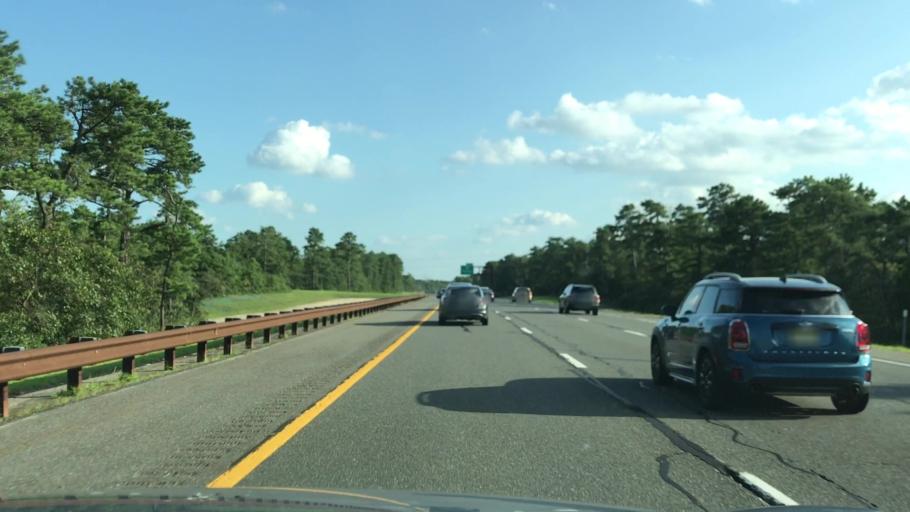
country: US
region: New Jersey
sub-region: Ocean County
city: Forked River
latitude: 39.8250
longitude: -74.2284
